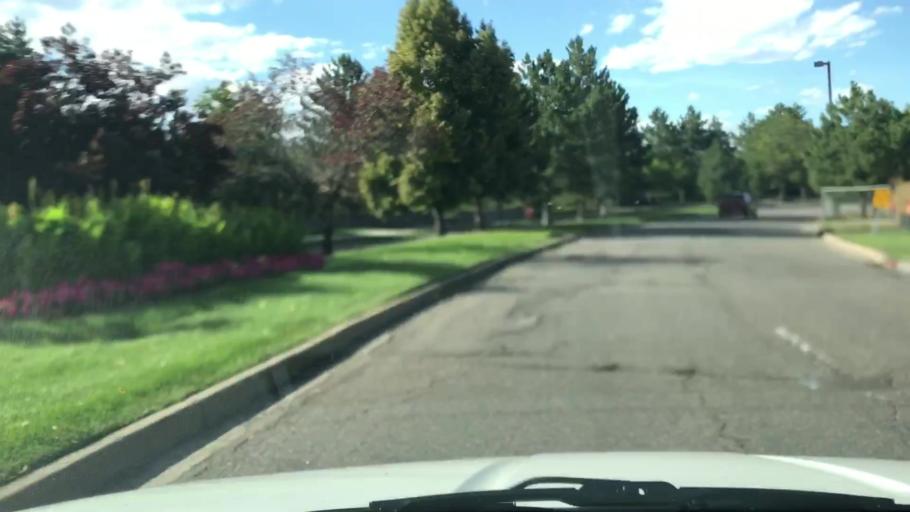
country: US
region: Colorado
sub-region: Arapahoe County
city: Greenwood Village
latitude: 39.6366
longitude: -104.9128
